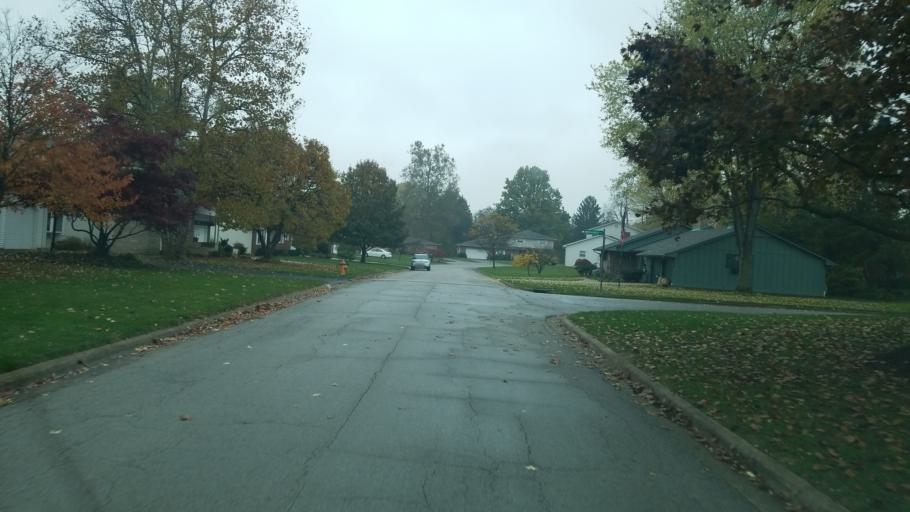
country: US
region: Ohio
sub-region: Franklin County
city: Upper Arlington
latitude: 40.0426
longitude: -83.0463
